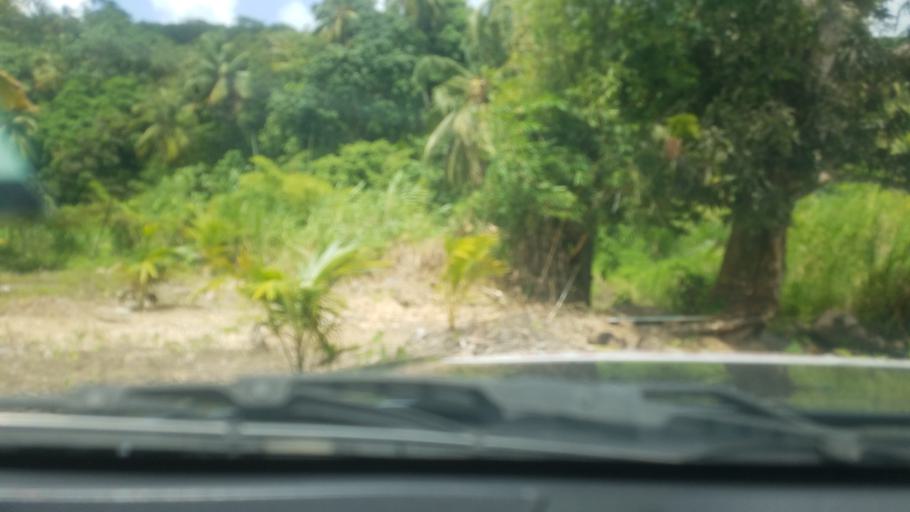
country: LC
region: Micoud Quarter
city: Micoud
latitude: 13.8035
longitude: -60.9535
